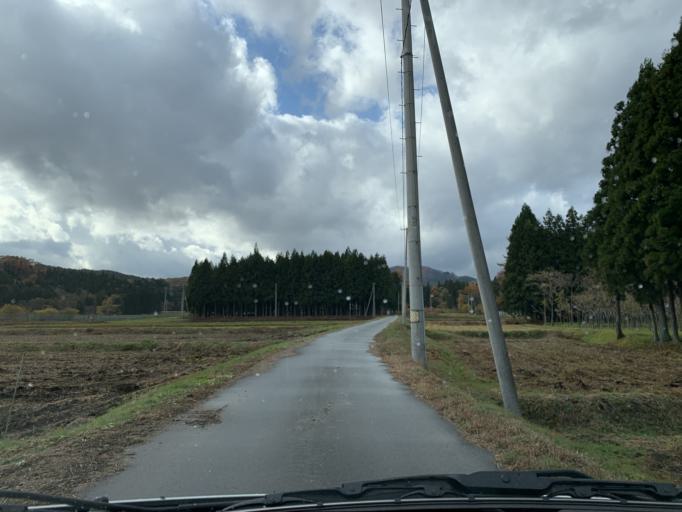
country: JP
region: Iwate
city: Mizusawa
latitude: 39.1179
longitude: 140.9571
